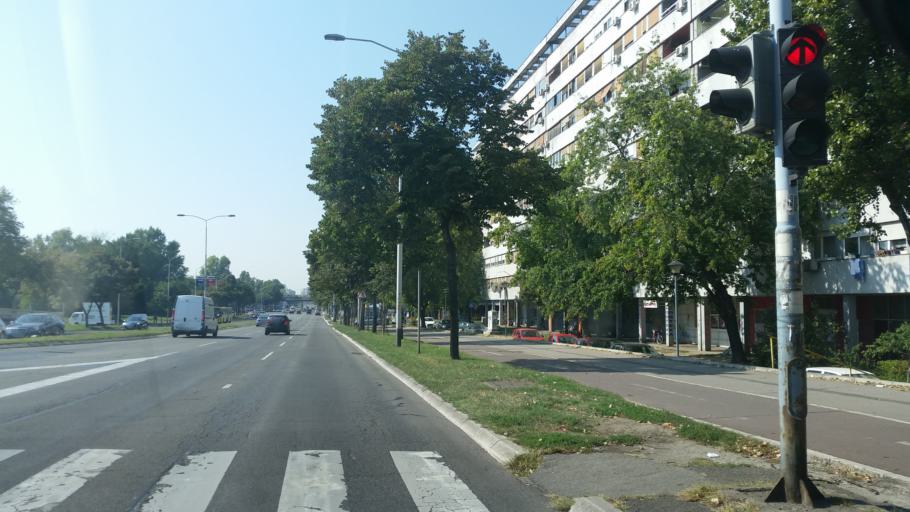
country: RS
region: Central Serbia
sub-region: Belgrade
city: Novi Beograd
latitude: 44.8175
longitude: 20.4069
